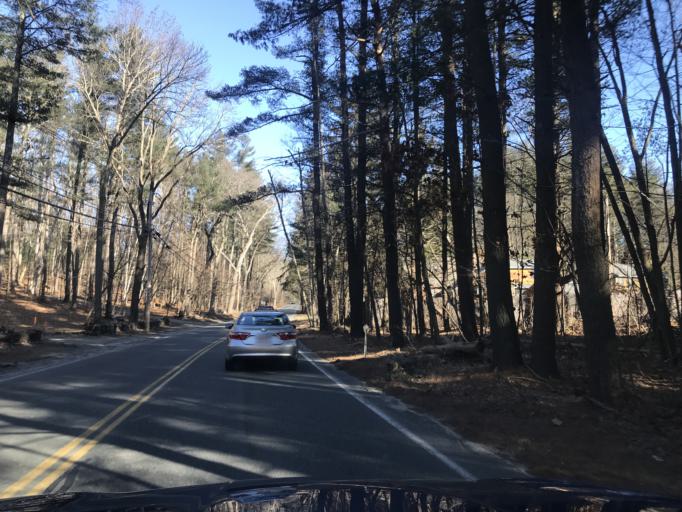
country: US
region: Massachusetts
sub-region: Essex County
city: Groveland
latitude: 42.7095
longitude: -71.0586
